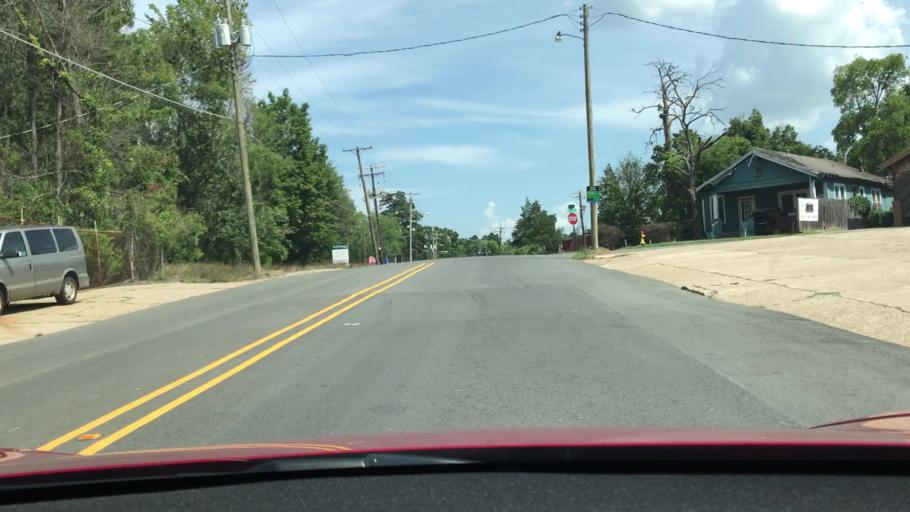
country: US
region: Louisiana
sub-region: Bossier Parish
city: Bossier City
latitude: 32.5021
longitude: -93.7350
